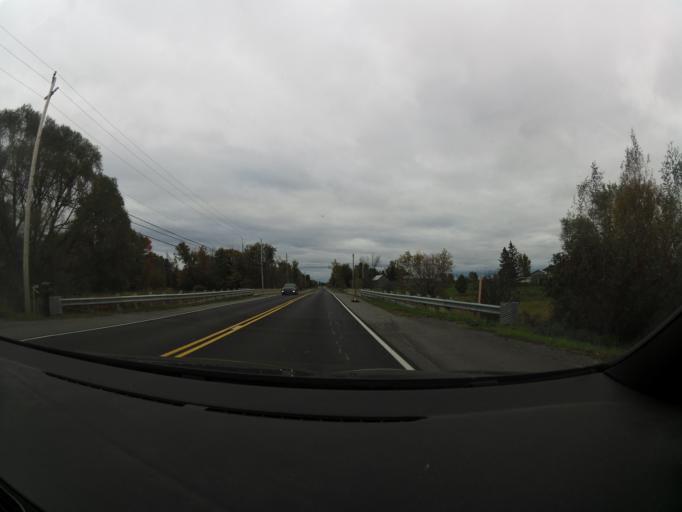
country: CA
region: Ontario
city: Bells Corners
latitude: 45.4139
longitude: -76.0105
